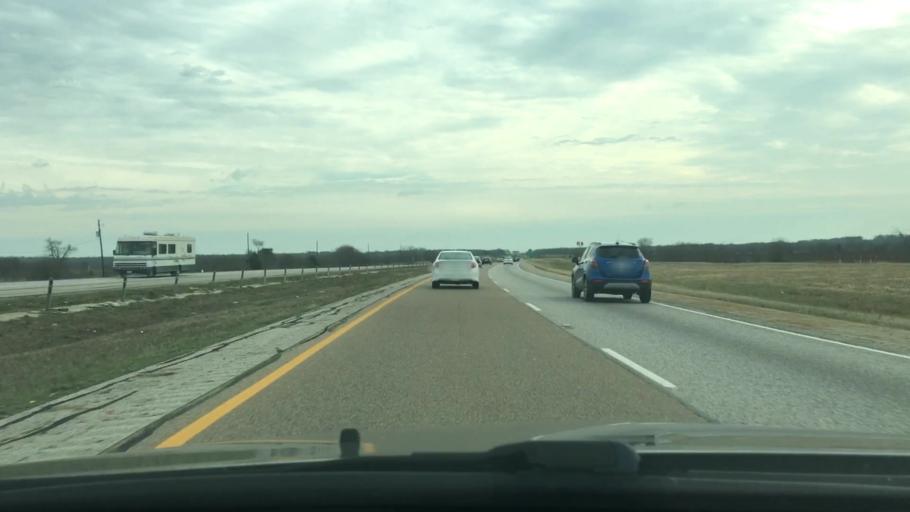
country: US
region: Texas
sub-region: Leon County
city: Centerville
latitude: 31.1046
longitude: -95.9653
